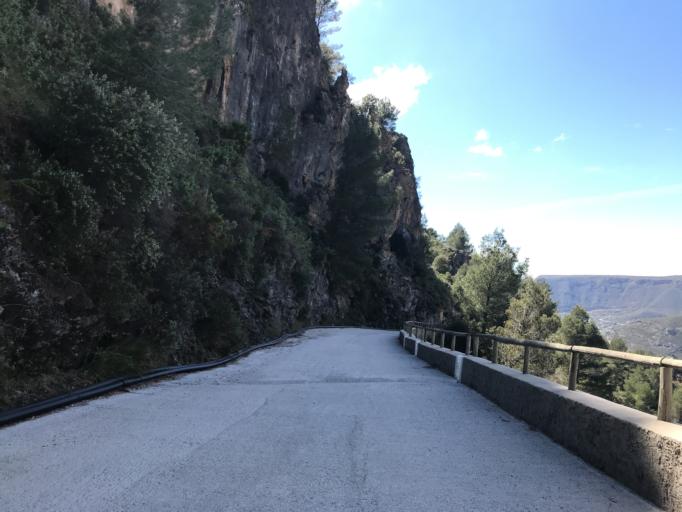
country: ES
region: Andalusia
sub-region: Provincia de Malaga
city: Alcaucin
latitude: 36.9171
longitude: -4.0980
